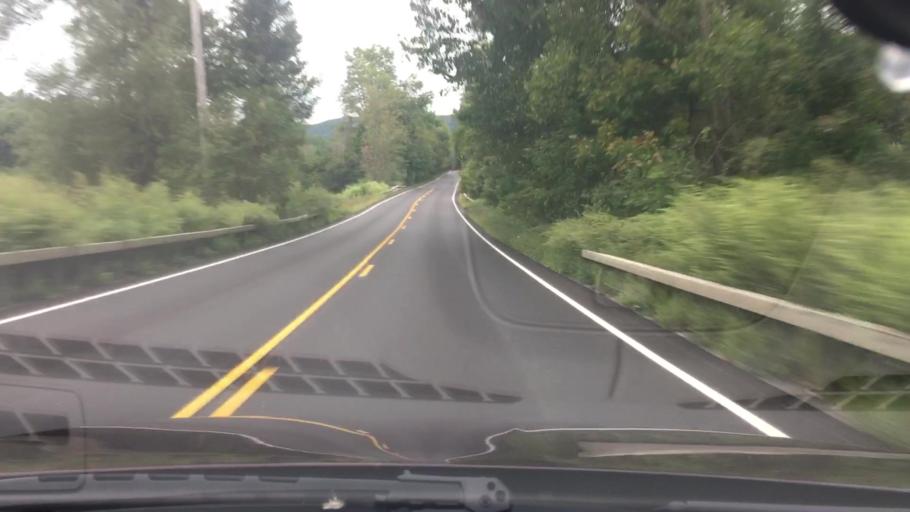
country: US
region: Connecticut
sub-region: Litchfield County
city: Kent
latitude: 41.8653
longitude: -73.5046
